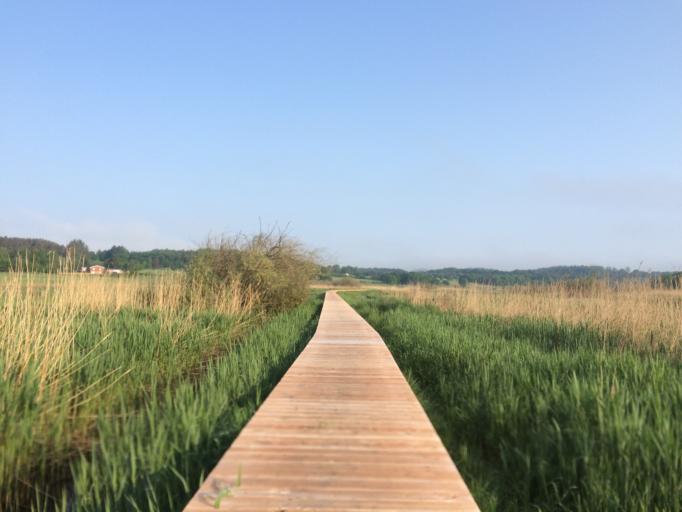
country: DK
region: Central Jutland
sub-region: Silkeborg Kommune
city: Svejbaek
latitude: 56.1944
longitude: 9.6547
